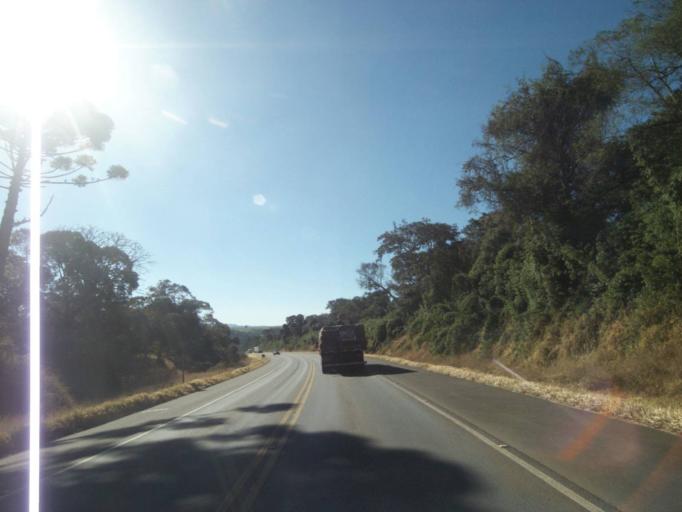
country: BR
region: Parana
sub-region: Tibagi
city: Tibagi
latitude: -24.6640
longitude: -50.4515
